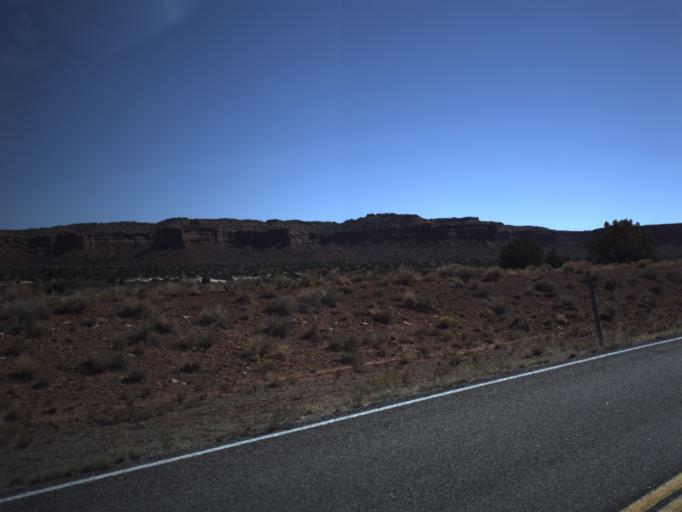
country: US
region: Utah
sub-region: San Juan County
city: Blanding
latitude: 37.6998
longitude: -110.2326
